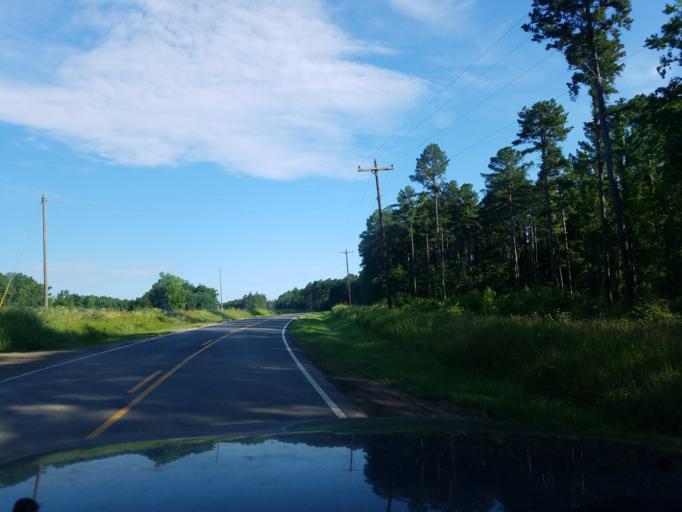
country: US
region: North Carolina
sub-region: Granville County
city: Butner
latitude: 36.1728
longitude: -78.7931
